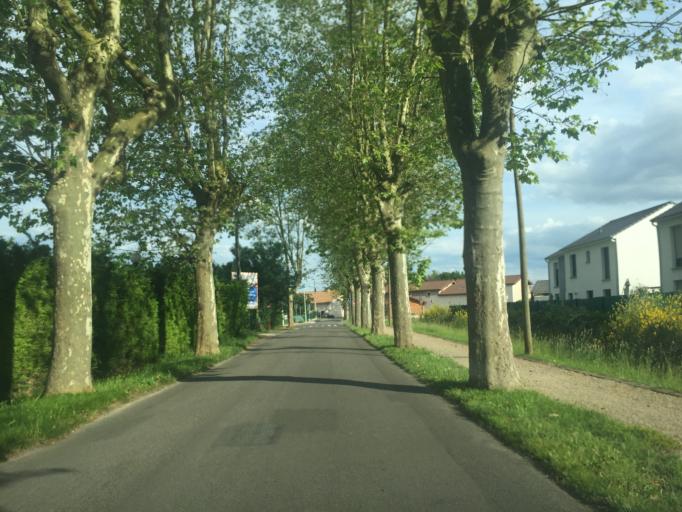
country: FR
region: Rhone-Alpes
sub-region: Departement de l'Ain
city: Thil
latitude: 45.8211
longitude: 5.0175
